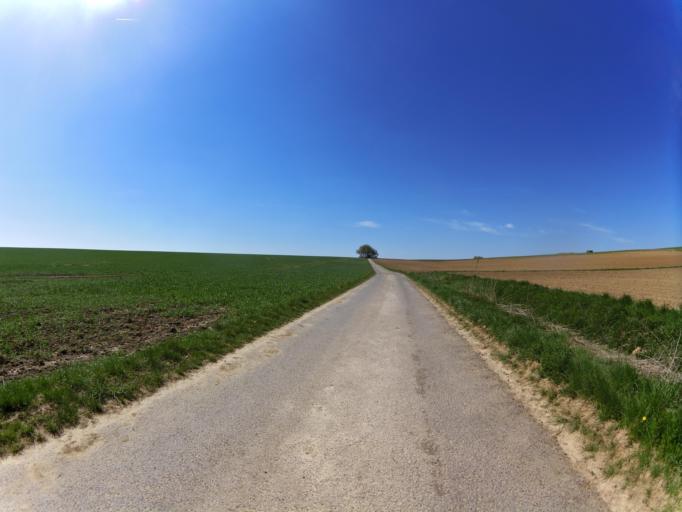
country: DE
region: Bavaria
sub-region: Regierungsbezirk Unterfranken
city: Winterhausen
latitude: 49.6897
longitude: 9.9887
